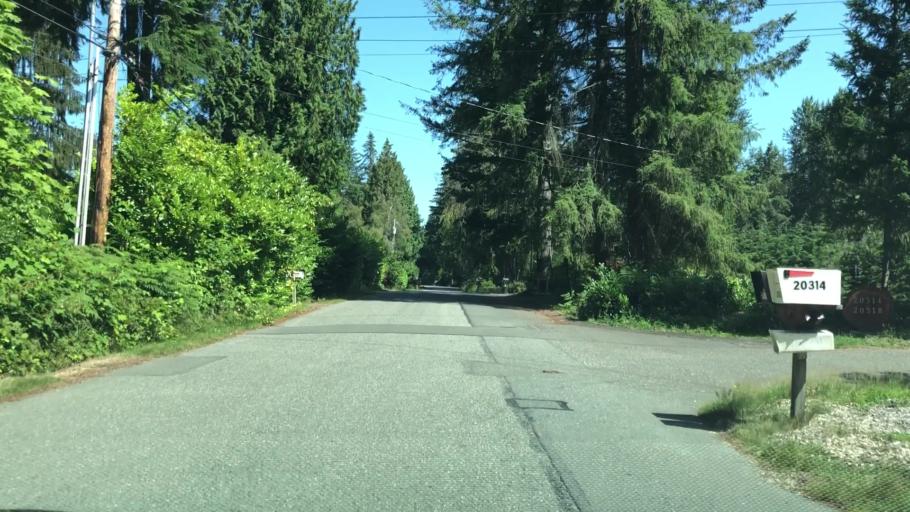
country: US
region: Washington
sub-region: Snohomish County
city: Maltby
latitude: 47.7745
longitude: -122.1184
